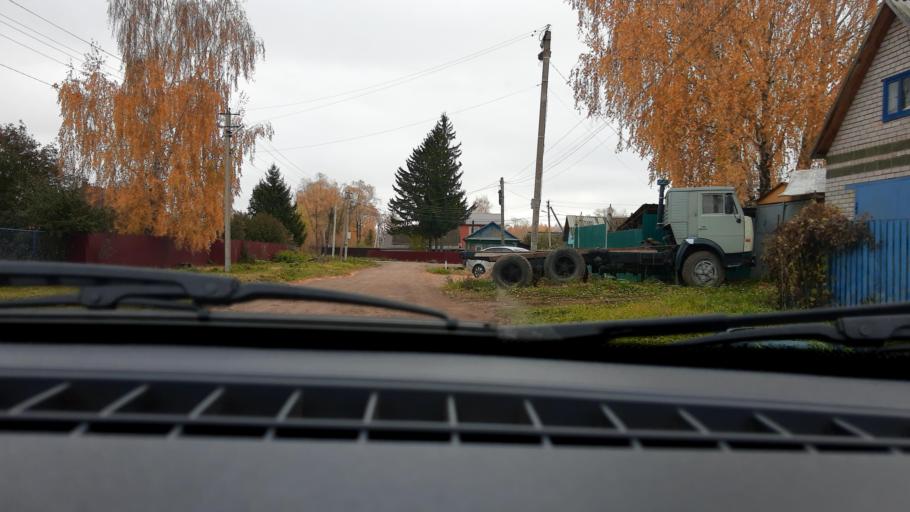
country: RU
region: Bashkortostan
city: Mikhaylovka
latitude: 54.7805
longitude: 55.8294
